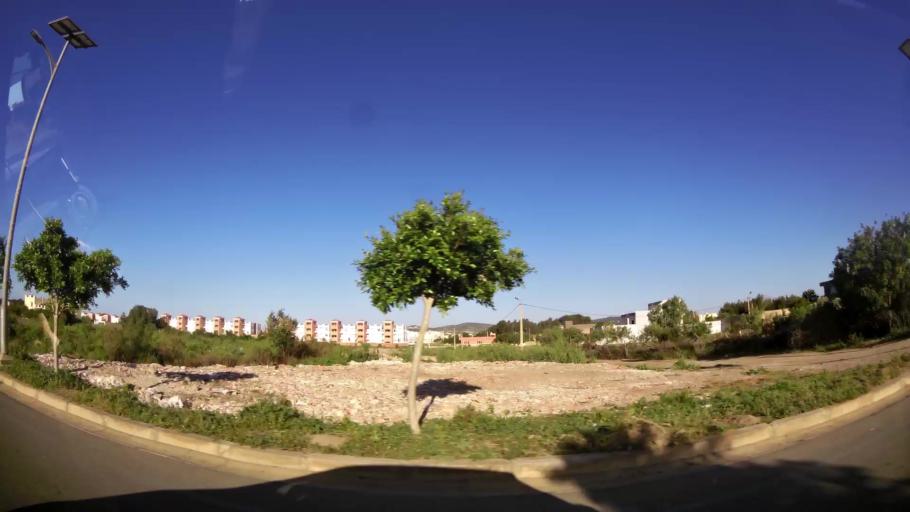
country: MA
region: Oriental
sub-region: Berkane-Taourirt
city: Madagh
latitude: 35.0804
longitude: -2.2442
